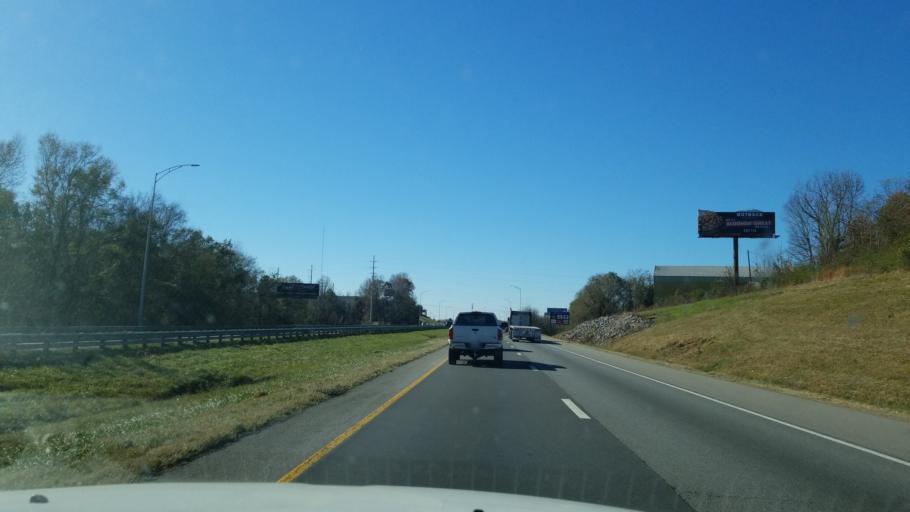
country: US
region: Alabama
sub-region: Tuscaloosa County
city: Tuscaloosa
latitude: 33.1741
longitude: -87.5134
